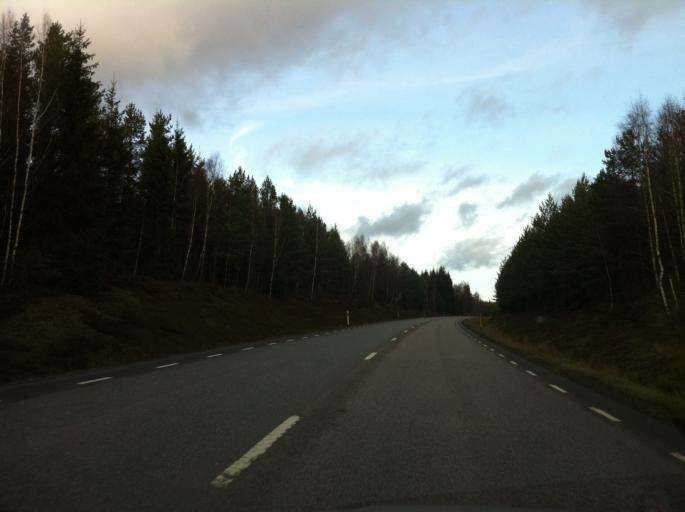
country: SE
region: Kronoberg
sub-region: Almhults Kommun
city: AElmhult
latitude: 56.5556
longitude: 14.1750
